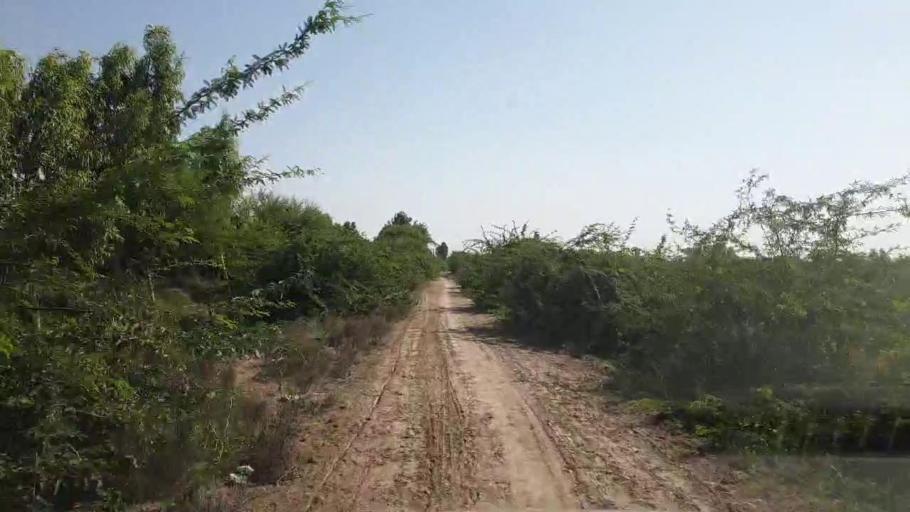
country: PK
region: Sindh
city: Kadhan
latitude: 24.5847
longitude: 69.0112
